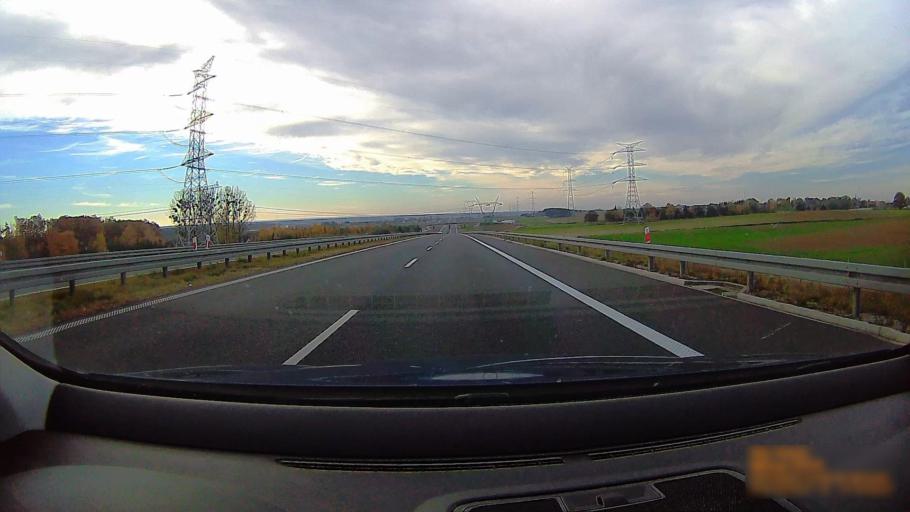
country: PL
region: Greater Poland Voivodeship
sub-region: Powiat ostrowski
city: Przygodzice
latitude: 51.6201
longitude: 17.8617
